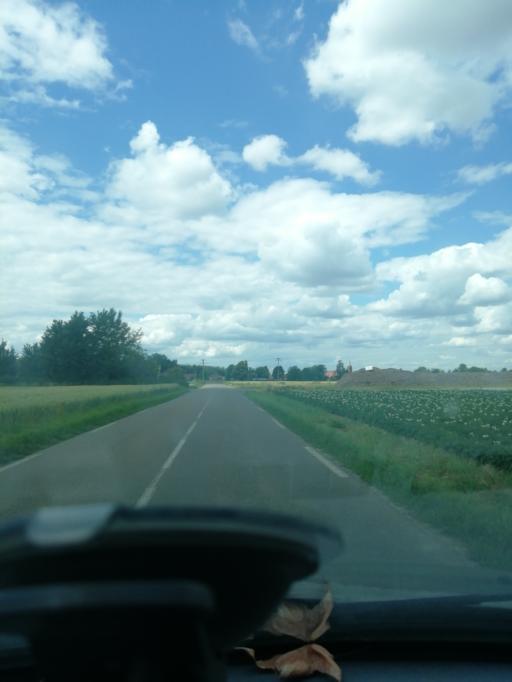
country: FR
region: Nord-Pas-de-Calais
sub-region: Departement du Nord
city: Lewarde
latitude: 50.3231
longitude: 3.1538
